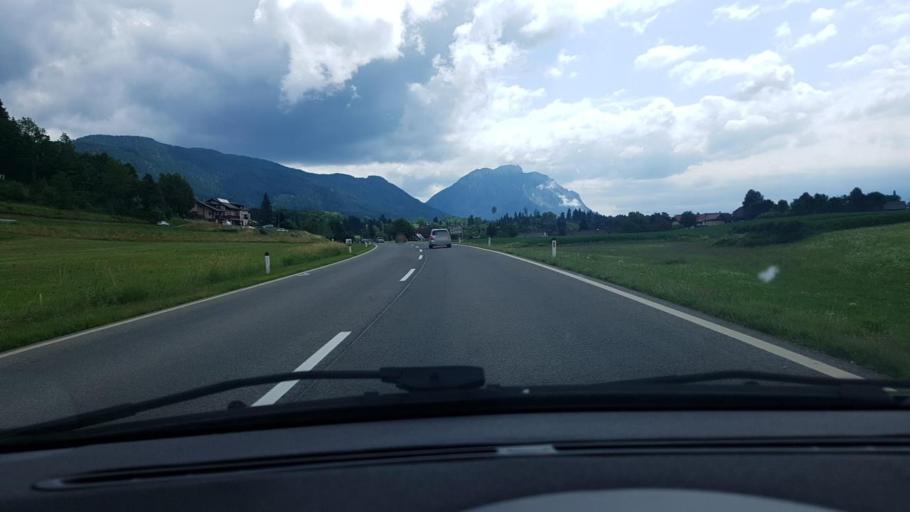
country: AT
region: Carinthia
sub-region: Politischer Bezirk Villach Land
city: Feistritz an der Gail
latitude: 46.6196
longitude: 13.5107
